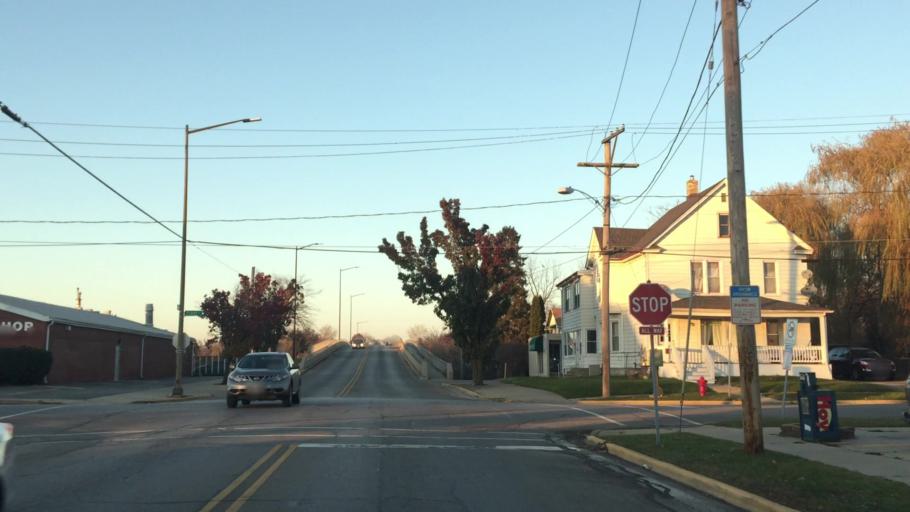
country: US
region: Illinois
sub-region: Kane County
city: Aurora
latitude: 41.7642
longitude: -88.3023
